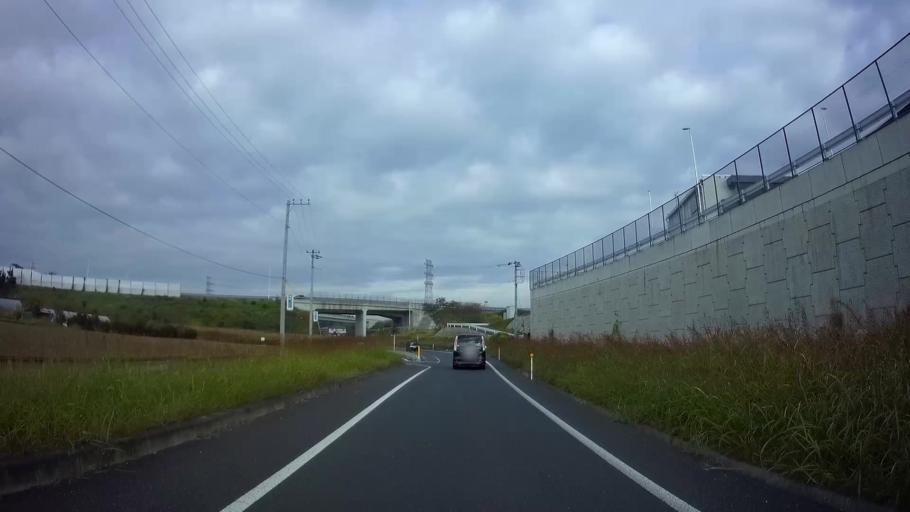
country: JP
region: Saitama
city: Okegawa
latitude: 35.9998
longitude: 139.5201
